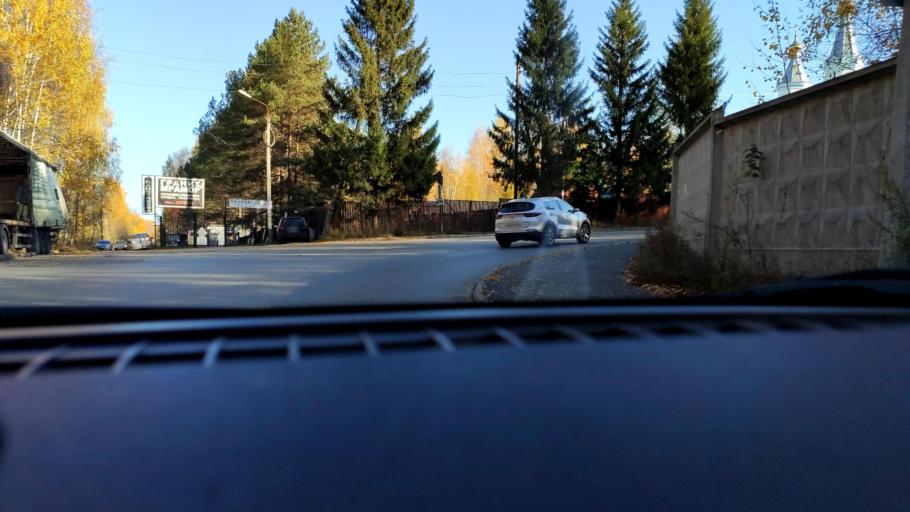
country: RU
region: Perm
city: Kondratovo
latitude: 58.0643
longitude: 56.1258
